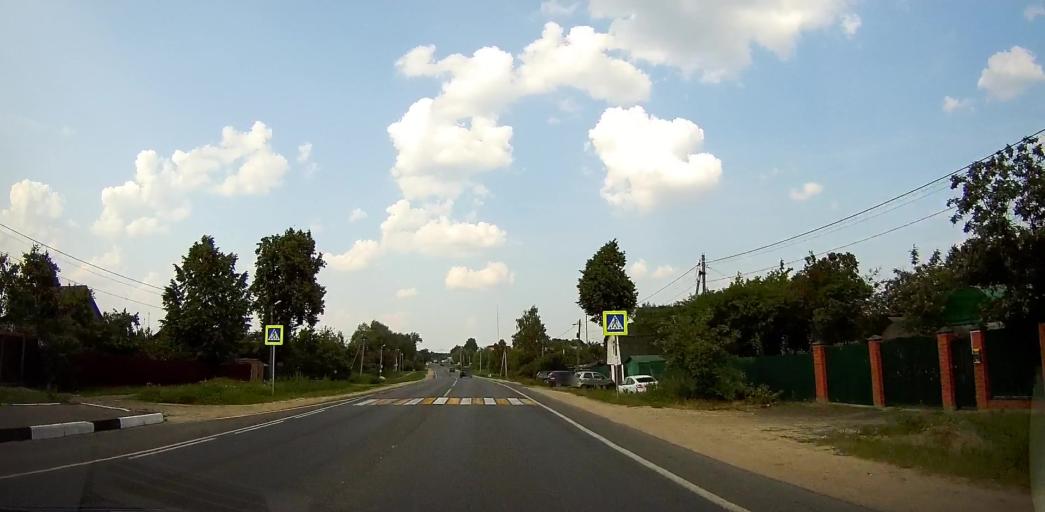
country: RU
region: Moskovskaya
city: Mikhnevo
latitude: 55.1315
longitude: 37.9489
